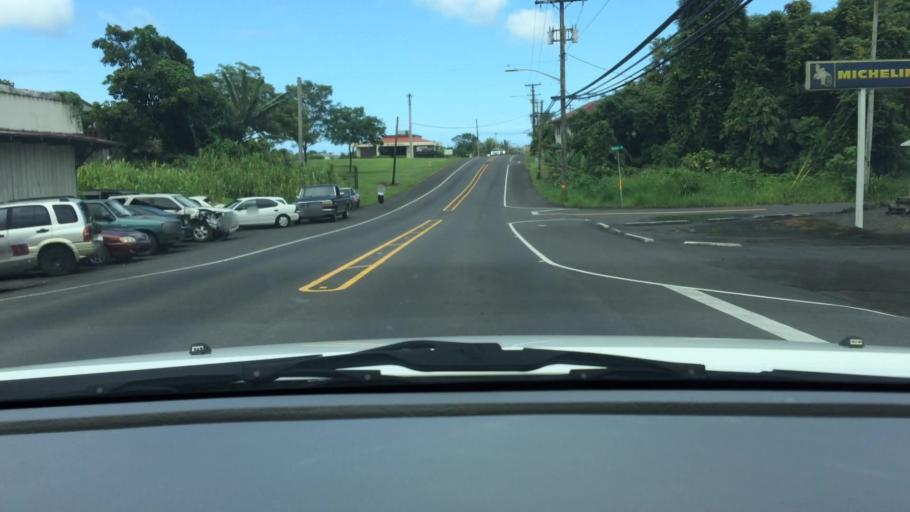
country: US
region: Hawaii
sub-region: Hawaii County
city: Hilo
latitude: 19.7117
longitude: -155.0748
